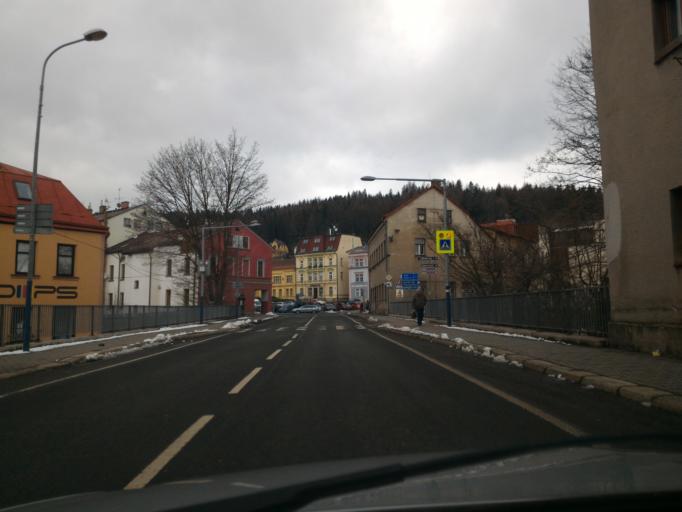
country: CZ
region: Liberecky
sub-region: Okres Jablonec nad Nisou
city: Smrzovka
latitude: 50.7386
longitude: 15.2460
